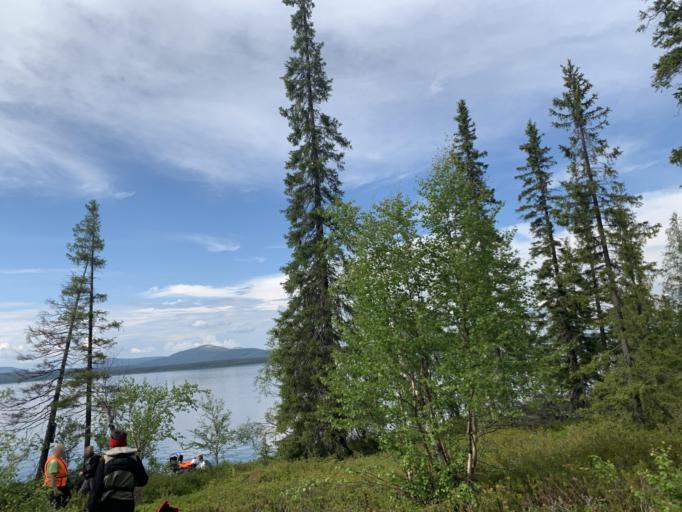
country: RU
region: Murmansk
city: Monchegorsk
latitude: 67.8023
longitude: 33.1027
